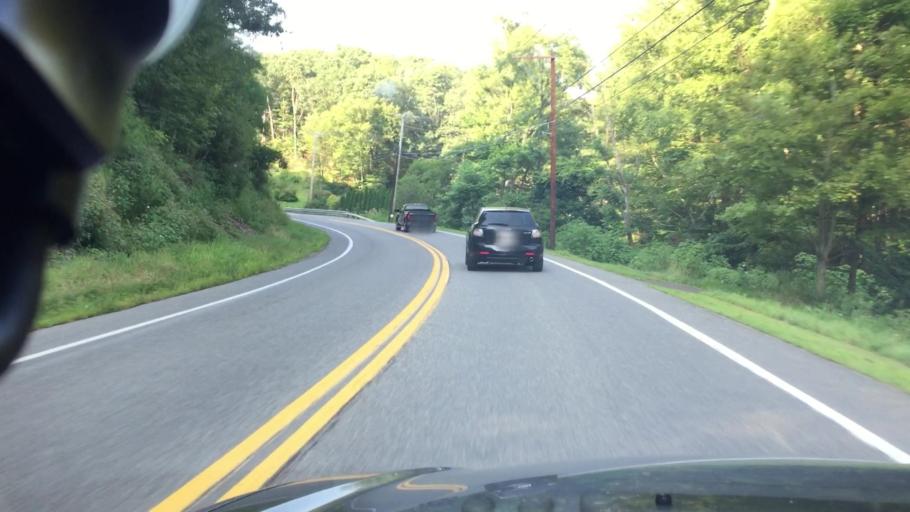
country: US
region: Pennsylvania
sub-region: Columbia County
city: Catawissa
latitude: 40.9127
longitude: -76.4744
